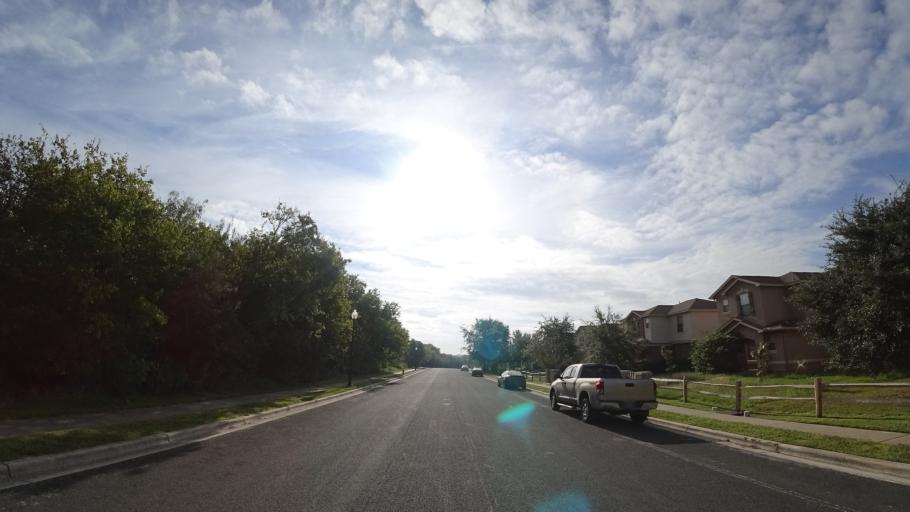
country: US
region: Texas
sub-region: Travis County
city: Austin
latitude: 30.1996
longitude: -97.7285
